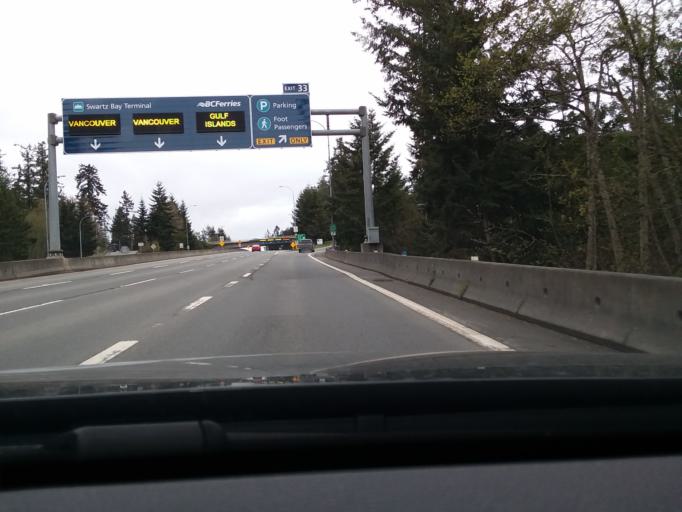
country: CA
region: British Columbia
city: North Saanich
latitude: 48.6819
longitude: -123.4150
